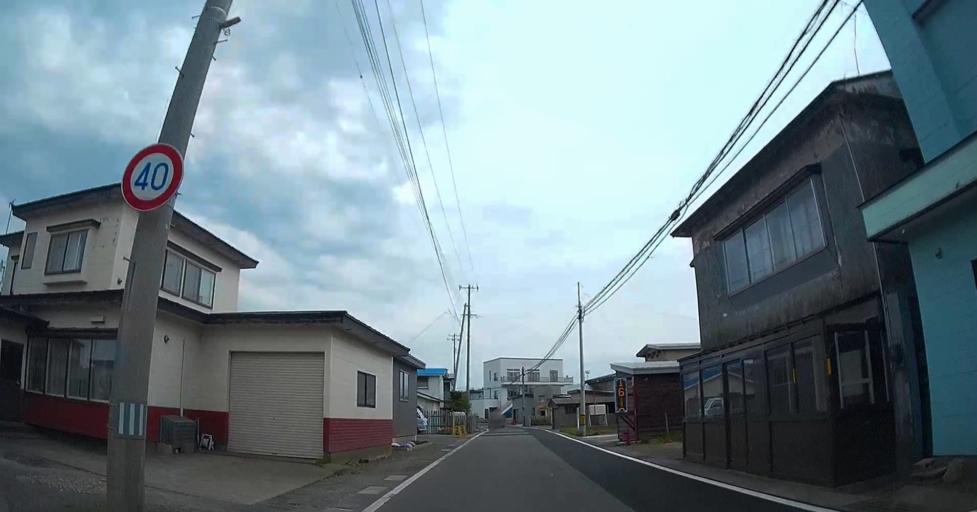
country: JP
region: Aomori
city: Shimokizukuri
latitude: 41.0342
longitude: 140.3293
